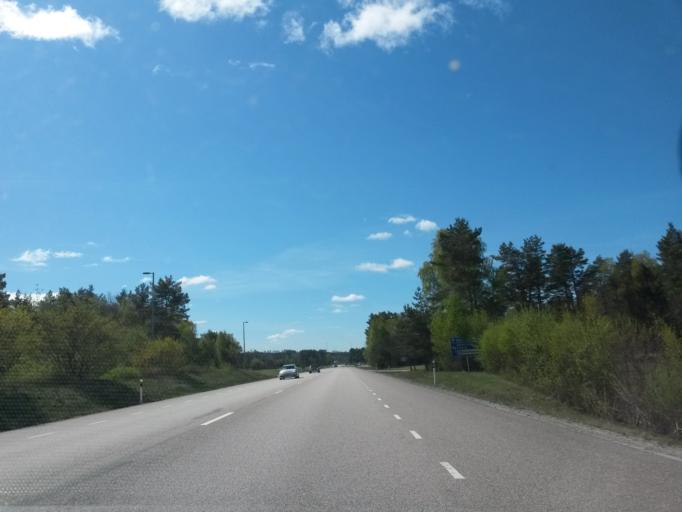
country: SE
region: Vaestra Goetaland
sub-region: Vargarda Kommun
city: Jonstorp
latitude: 57.9843
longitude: 12.6908
